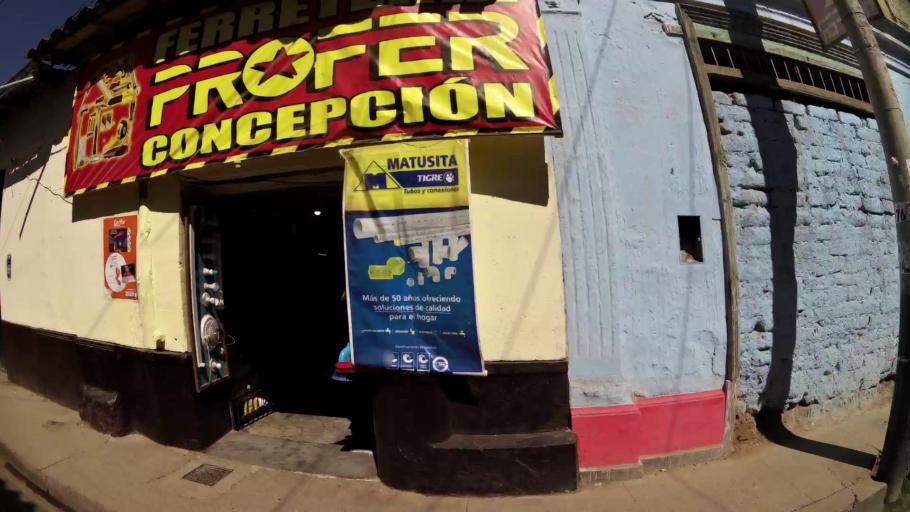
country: PE
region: Junin
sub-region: Provincia de Concepcion
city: Concepcion
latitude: -11.9195
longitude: -75.3129
